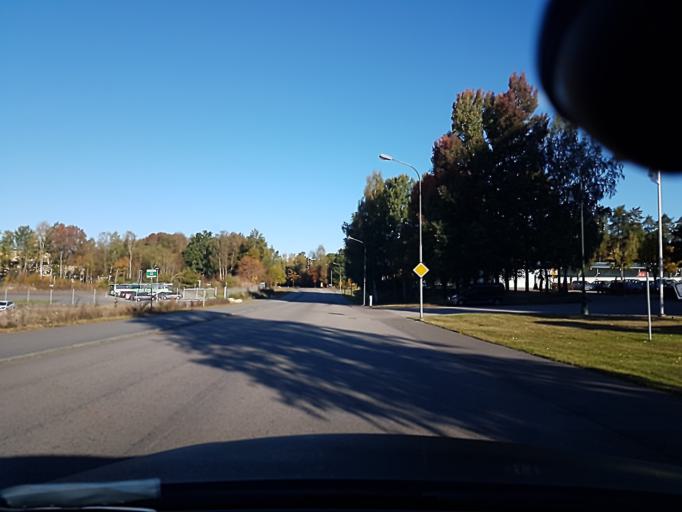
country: SE
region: Kronoberg
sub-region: Vaxjo Kommun
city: Vaexjoe
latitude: 56.8691
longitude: 14.8363
